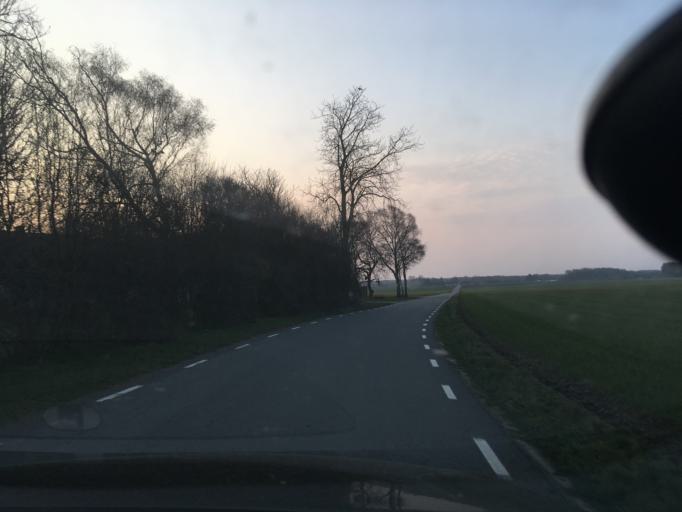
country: SE
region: Skane
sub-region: Ystads Kommun
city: Kopingebro
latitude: 55.4095
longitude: 14.1540
